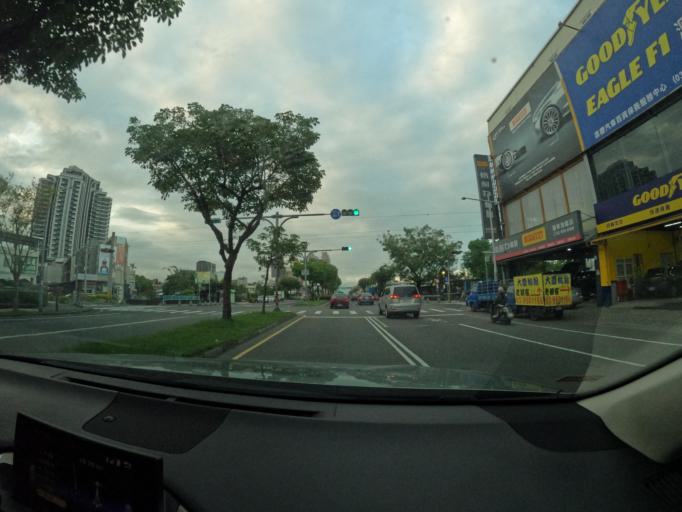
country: TW
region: Taiwan
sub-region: Yilan
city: Yilan
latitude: 24.6721
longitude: 121.7778
